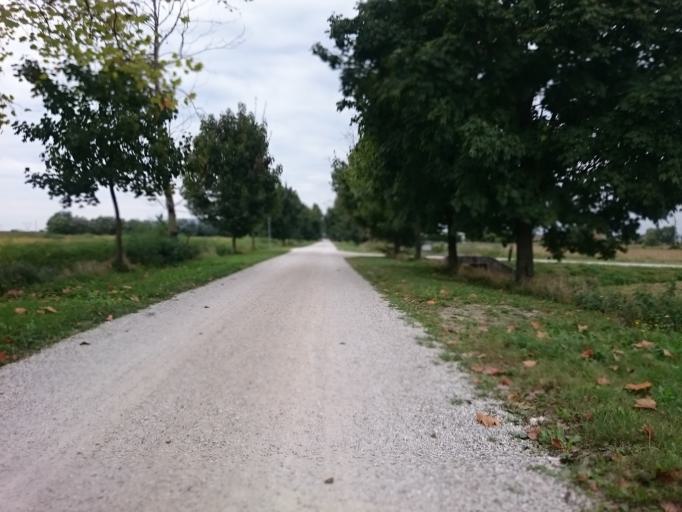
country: IT
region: Veneto
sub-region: Provincia di Vicenza
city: Grumolo delle Abbadesse
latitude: 45.4974
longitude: 11.6604
